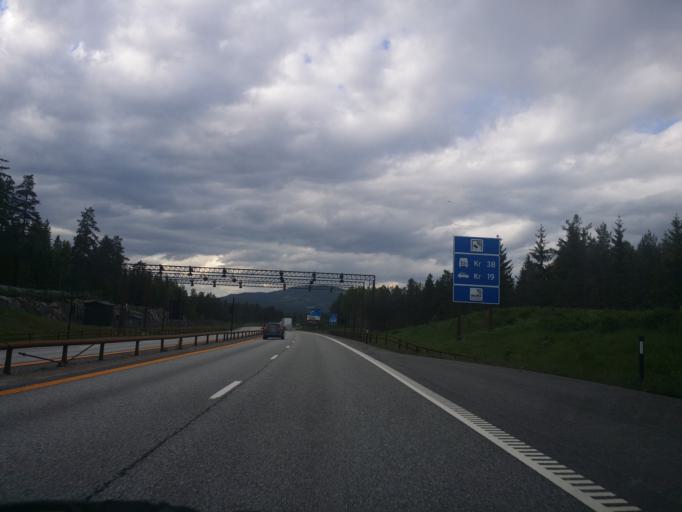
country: NO
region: Akershus
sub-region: Eidsvoll
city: Raholt
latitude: 60.3058
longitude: 11.1414
